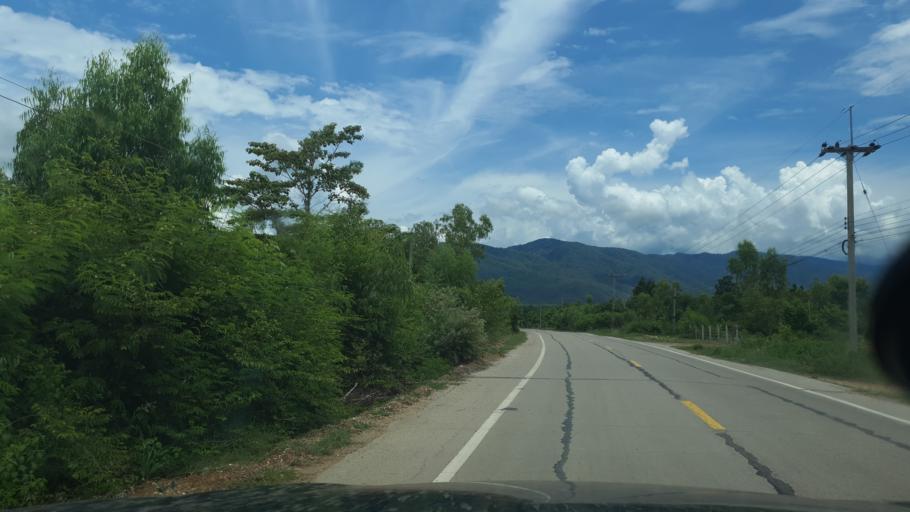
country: TH
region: Lampang
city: Sop Prap
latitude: 17.9176
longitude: 99.4112
